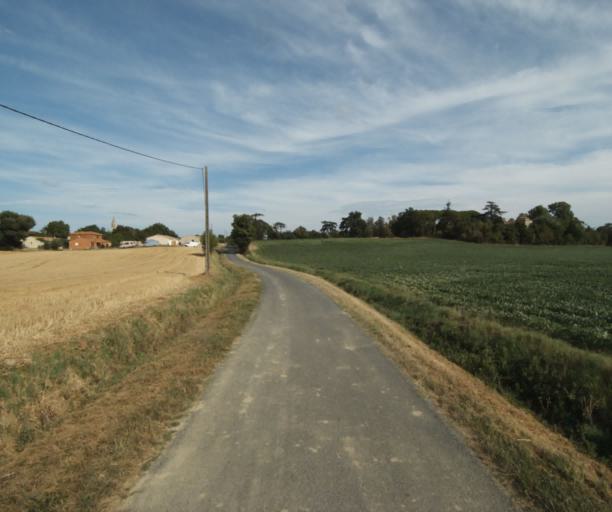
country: FR
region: Midi-Pyrenees
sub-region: Departement de la Haute-Garonne
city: Revel
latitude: 43.5048
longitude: 1.9923
